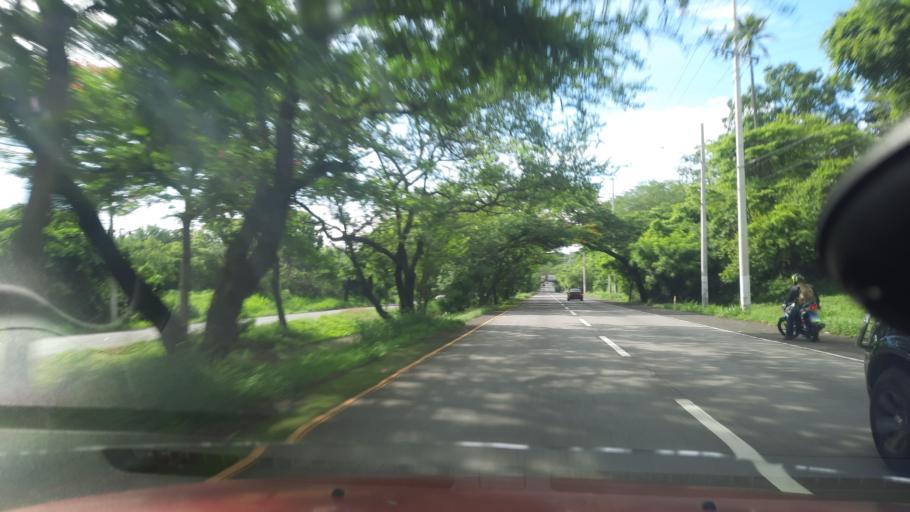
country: SV
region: La Paz
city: El Rosario
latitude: 13.4987
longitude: -89.0782
